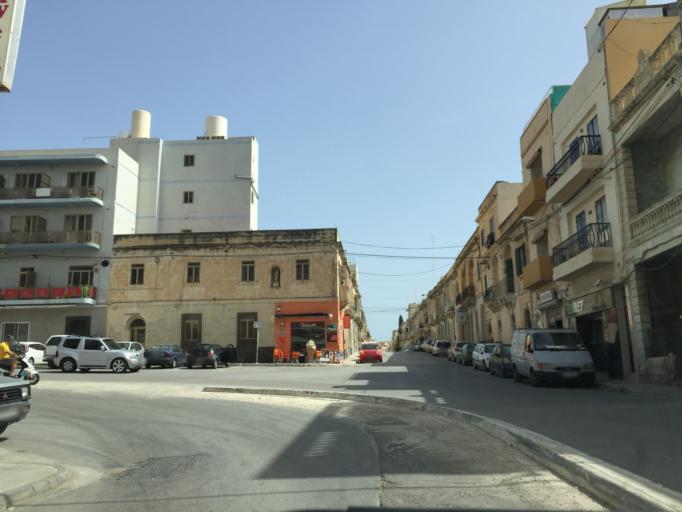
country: MT
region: Birzebbuga
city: Birzebbuga
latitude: 35.8237
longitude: 14.5284
